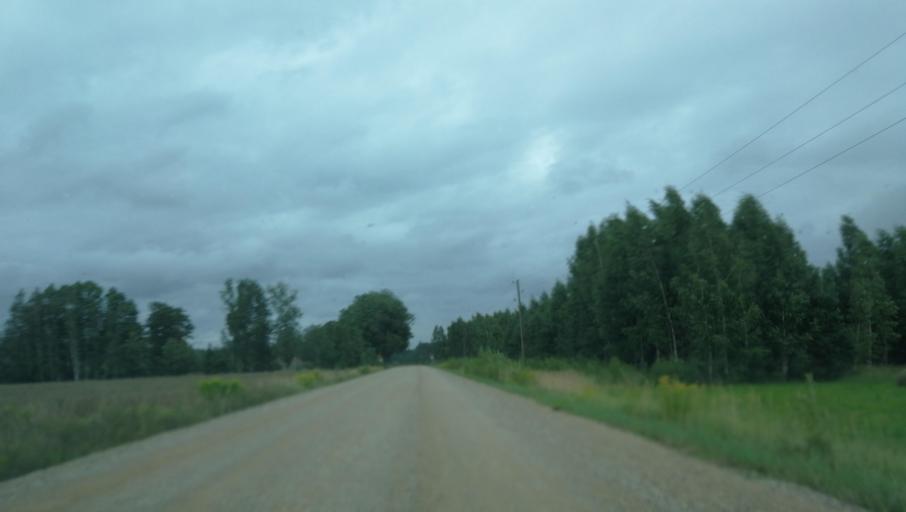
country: LV
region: Beverina
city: Murmuiza
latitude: 57.4129
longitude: 25.5127
